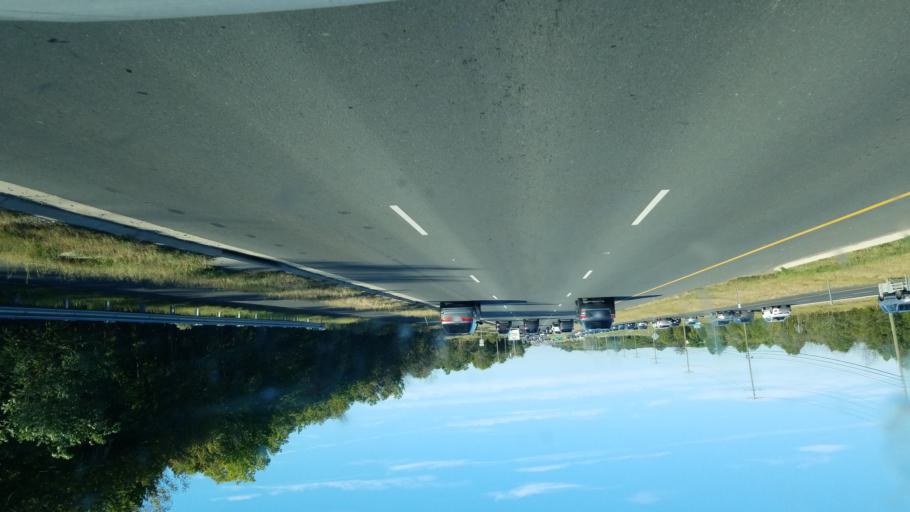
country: US
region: Virginia
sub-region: Fairfax County
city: Chantilly
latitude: 38.9080
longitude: -77.4657
